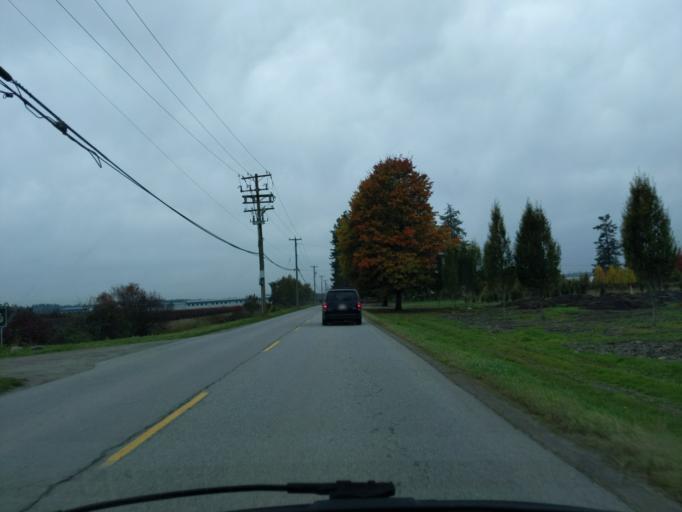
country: CA
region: British Columbia
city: Pitt Meadows
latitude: 49.2225
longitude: -122.7088
